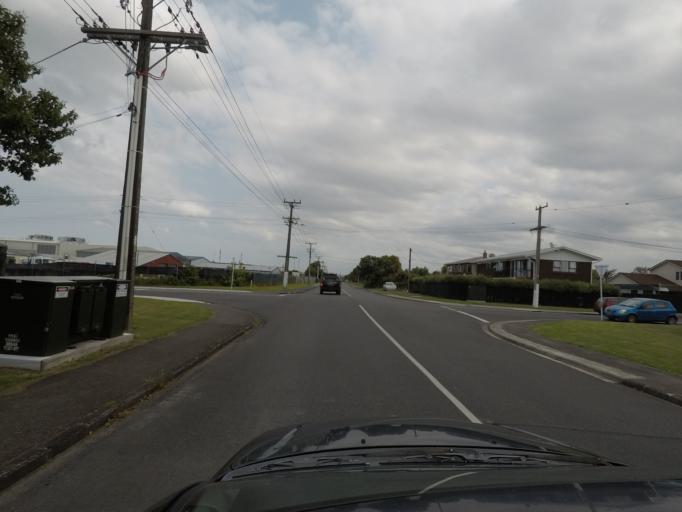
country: NZ
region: Auckland
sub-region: Auckland
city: Rosebank
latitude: -36.8286
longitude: 174.6465
